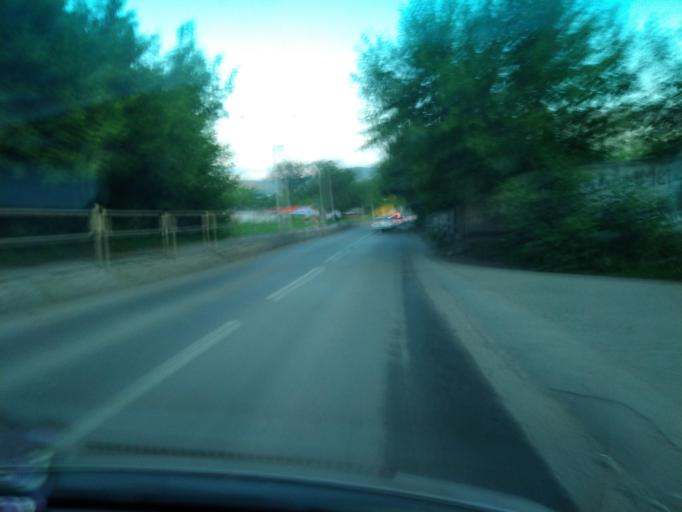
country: RU
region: Krasnoyarskiy
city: Krasnoyarsk
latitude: 55.9852
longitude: 92.8712
